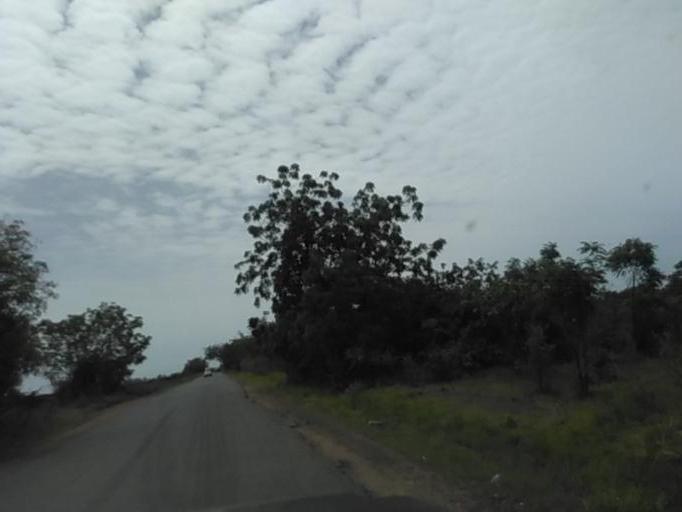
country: GH
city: Akropong
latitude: 6.0931
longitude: 0.0774
